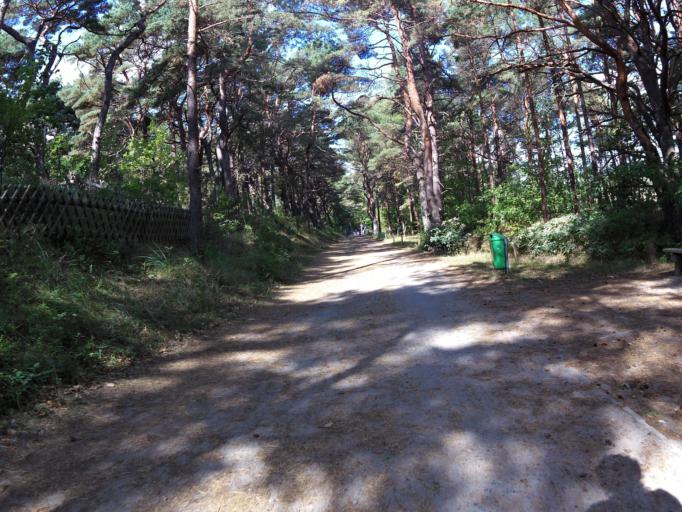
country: DE
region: Mecklenburg-Vorpommern
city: Ostseebad Zinnowitz
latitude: 54.0943
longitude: 13.8831
